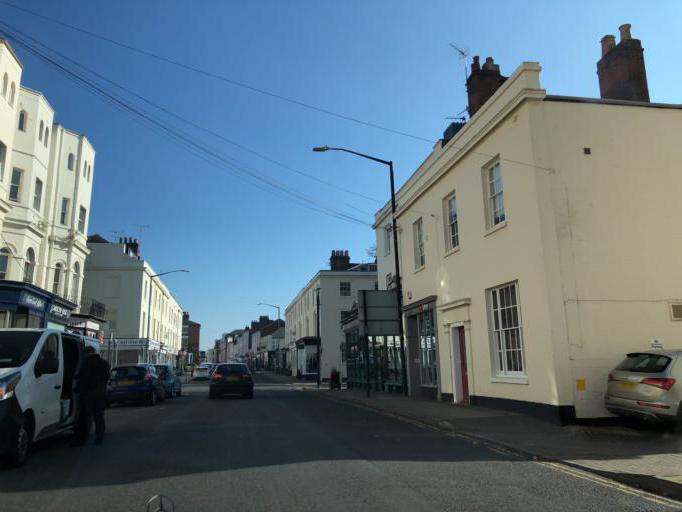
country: GB
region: England
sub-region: Warwickshire
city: Royal Leamington Spa
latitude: 52.2902
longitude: -1.5395
